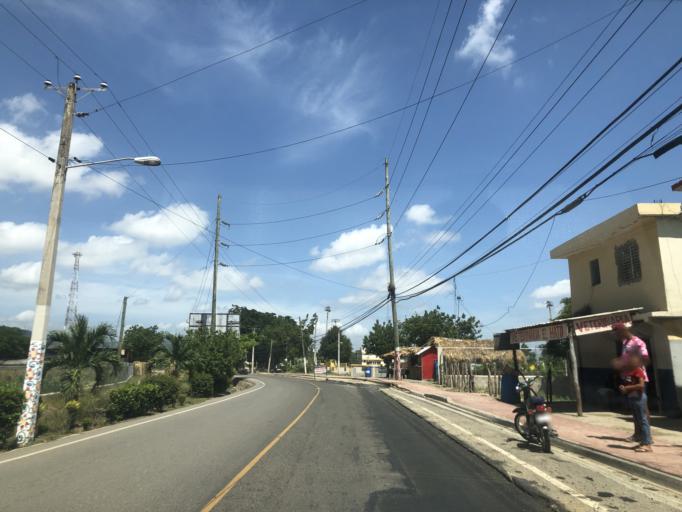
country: DO
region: Santiago
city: La Canela
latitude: 19.4511
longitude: -70.7763
